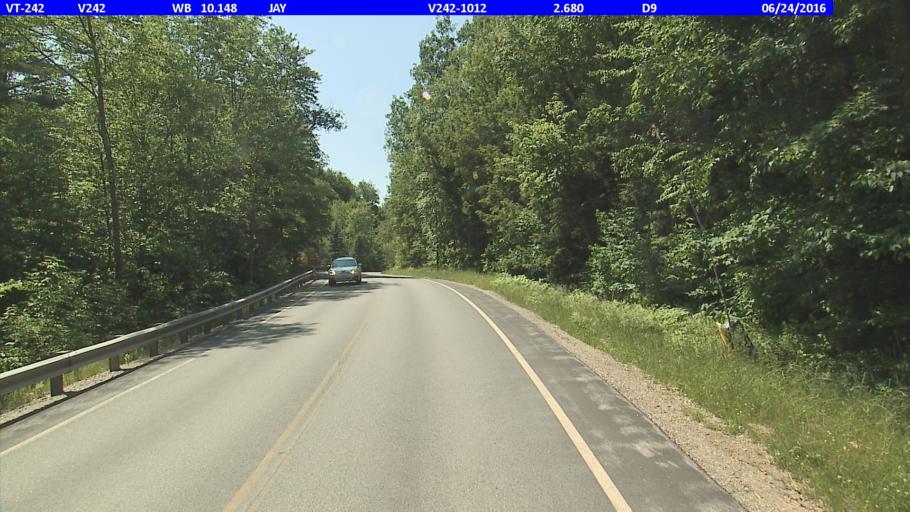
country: US
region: Vermont
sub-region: Franklin County
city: Richford
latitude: 44.9397
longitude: -72.4602
